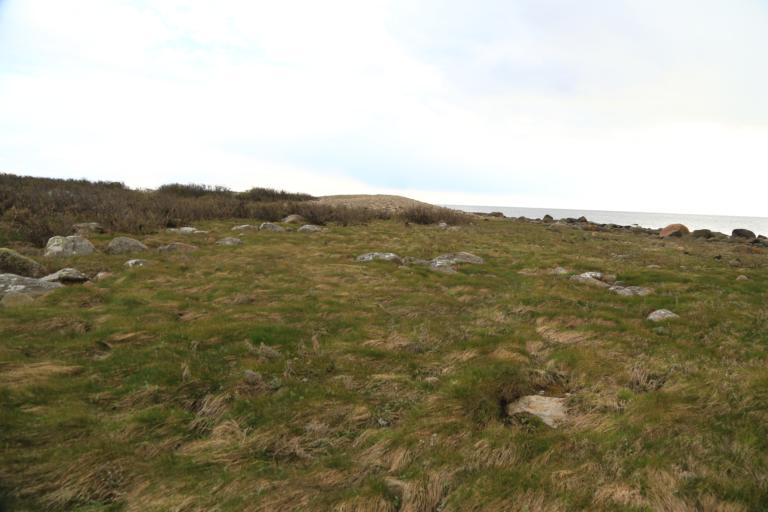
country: SE
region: Halland
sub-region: Varbergs Kommun
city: Traslovslage
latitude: 57.0520
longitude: 12.2689
